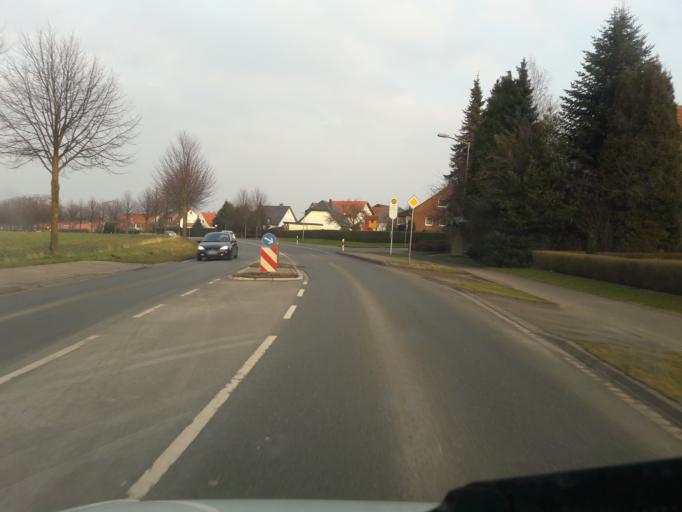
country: DE
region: North Rhine-Westphalia
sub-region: Regierungsbezirk Detmold
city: Hille
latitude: 52.2995
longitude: 8.7223
